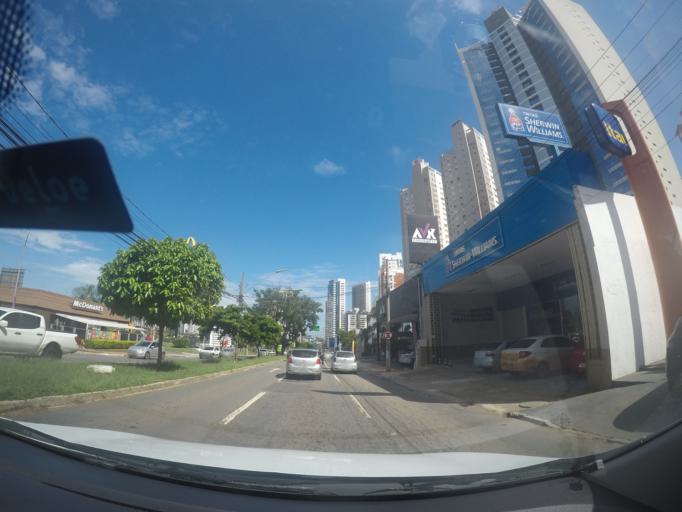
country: BR
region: Goias
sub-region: Goiania
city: Goiania
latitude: -16.7076
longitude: -49.2366
